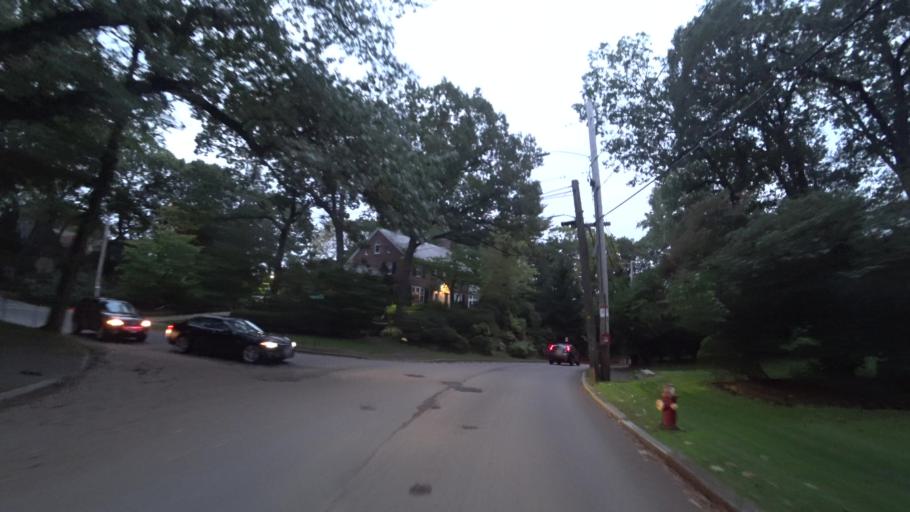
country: US
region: Massachusetts
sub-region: Middlesex County
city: Newton
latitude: 42.3347
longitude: -71.1814
